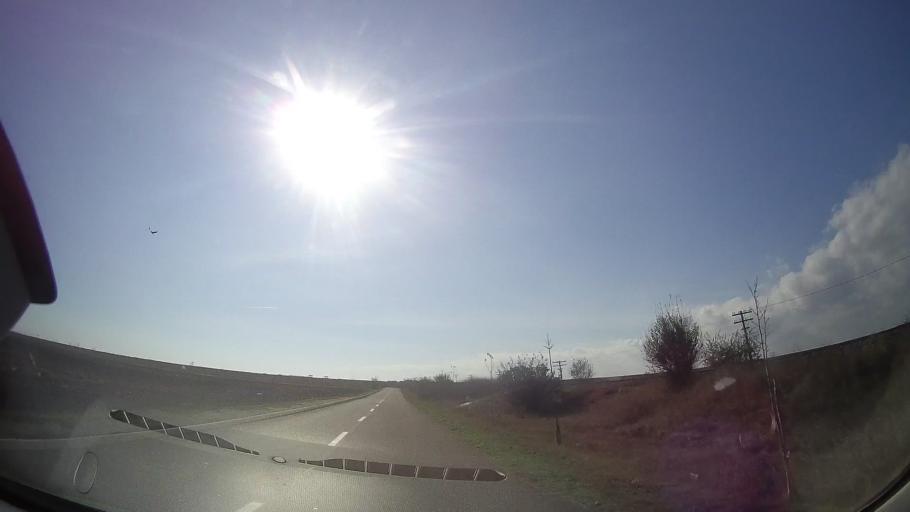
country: RO
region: Constanta
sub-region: Comuna Costinesti
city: Schitu
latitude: 43.9237
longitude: 28.6322
